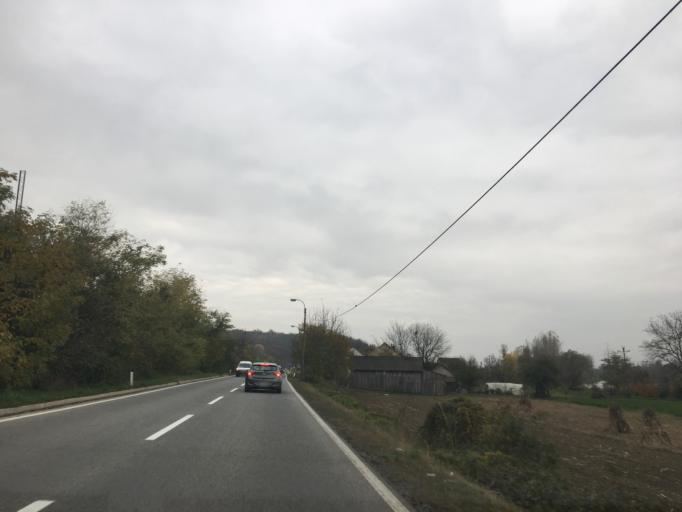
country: RS
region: Central Serbia
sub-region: Raski Okrug
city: Kraljevo
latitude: 43.7204
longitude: 20.7749
